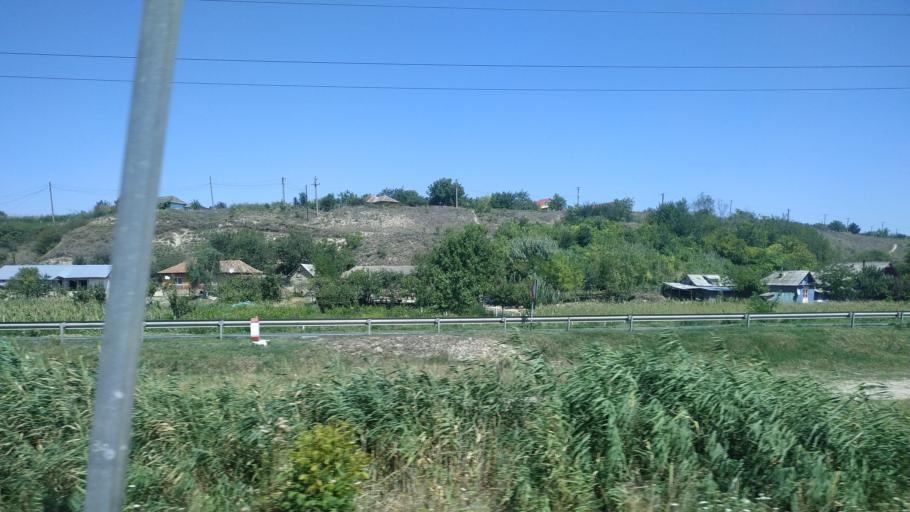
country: RO
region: Constanta
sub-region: Comuna Saligny
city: Saligny
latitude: 44.2763
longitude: 28.0881
